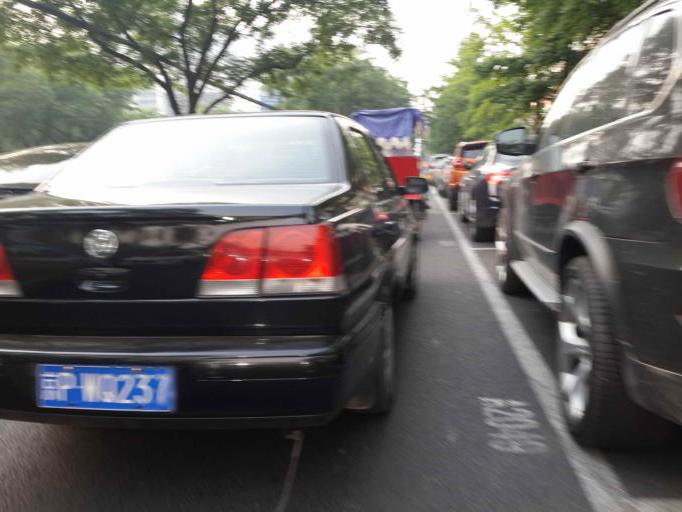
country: CN
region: Beijing
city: Chaowai
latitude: 39.9310
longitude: 116.4444
